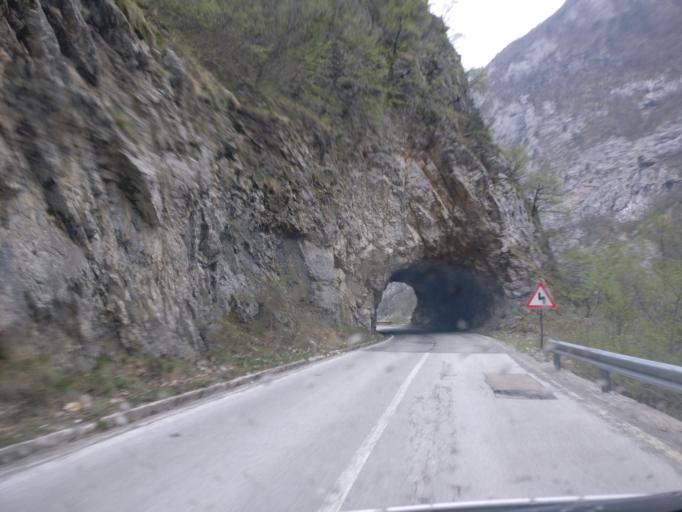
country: ME
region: Opstina Pluzine
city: Pluzine
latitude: 43.2335
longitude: 18.8456
